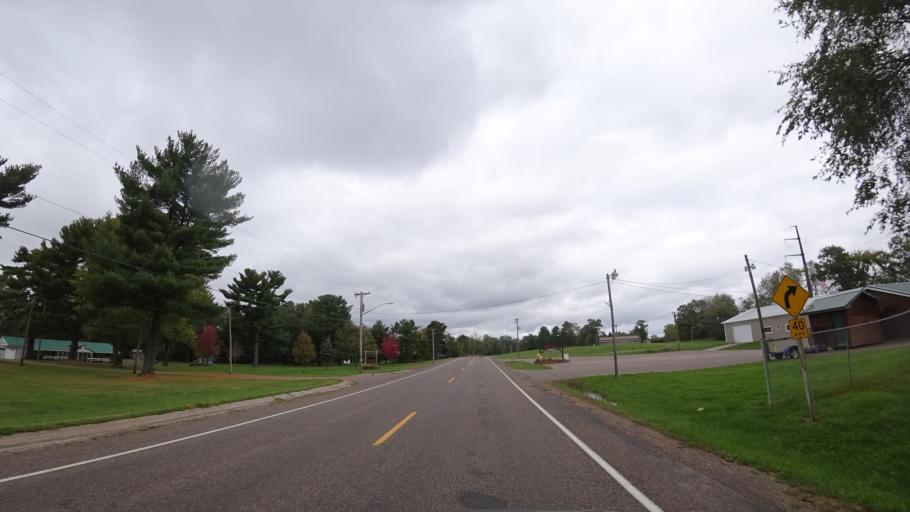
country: US
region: Wisconsin
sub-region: Chippewa County
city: Lake Wissota
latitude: 45.0286
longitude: -91.2870
